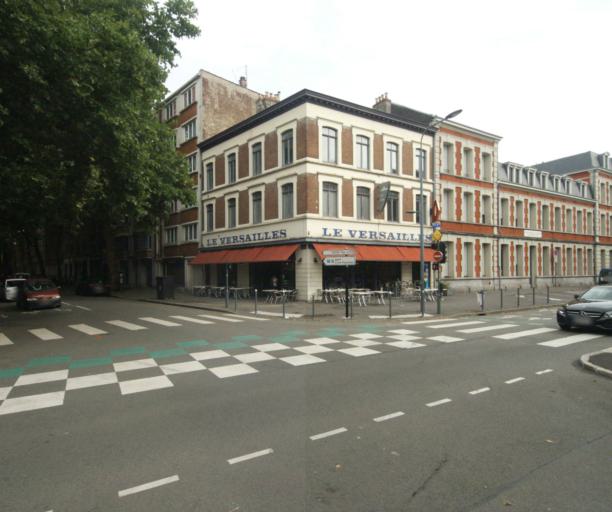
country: FR
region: Nord-Pas-de-Calais
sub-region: Departement du Nord
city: Lille
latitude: 50.6288
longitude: 3.0737
